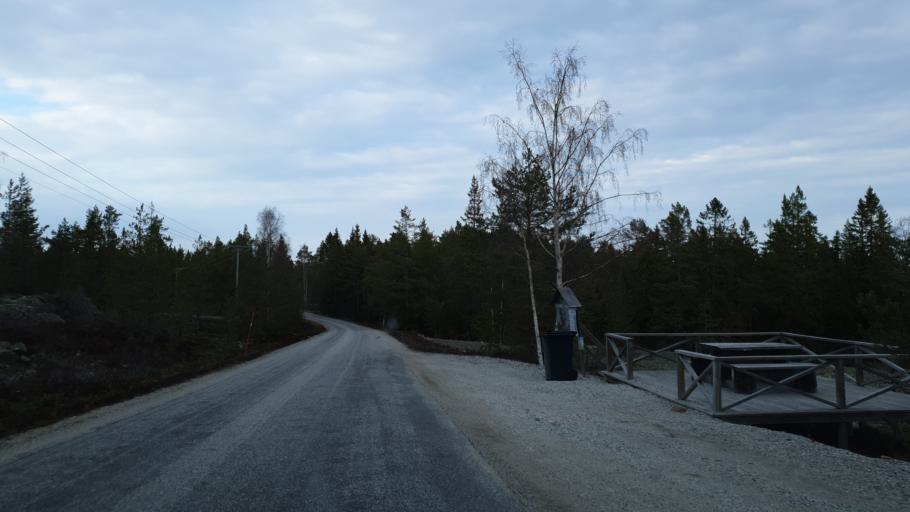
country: SE
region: Vaesternorrland
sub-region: Sundsvalls Kommun
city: Njurundabommen
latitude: 61.9687
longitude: 17.3810
